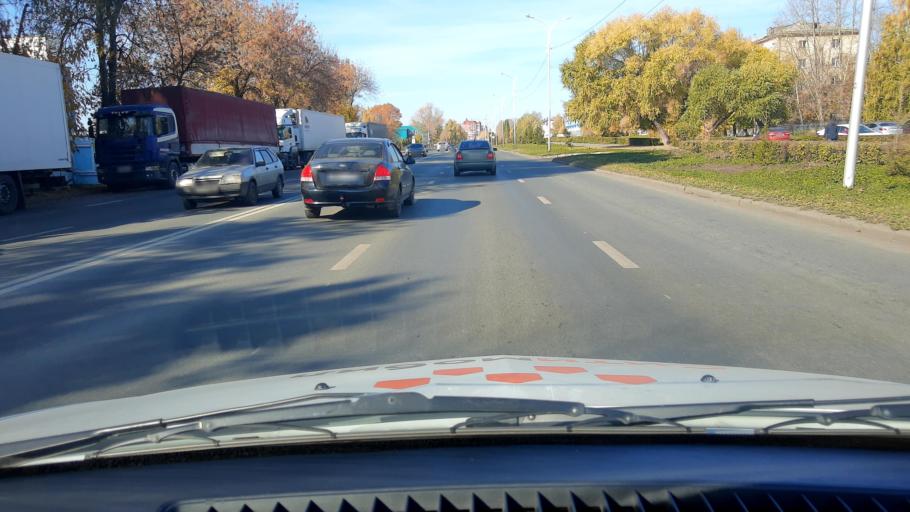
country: RU
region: Bashkortostan
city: Ufa
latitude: 54.8055
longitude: 56.1046
